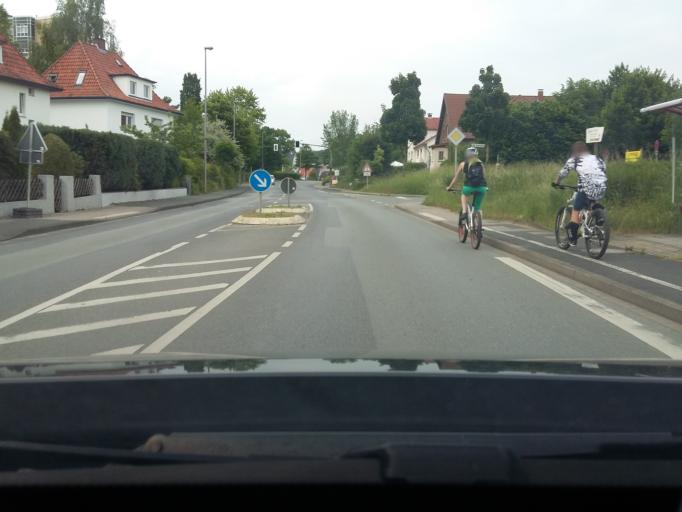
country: DE
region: North Rhine-Westphalia
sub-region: Regierungsbezirk Detmold
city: Bad Salzuflen
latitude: 52.0926
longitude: 8.7615
